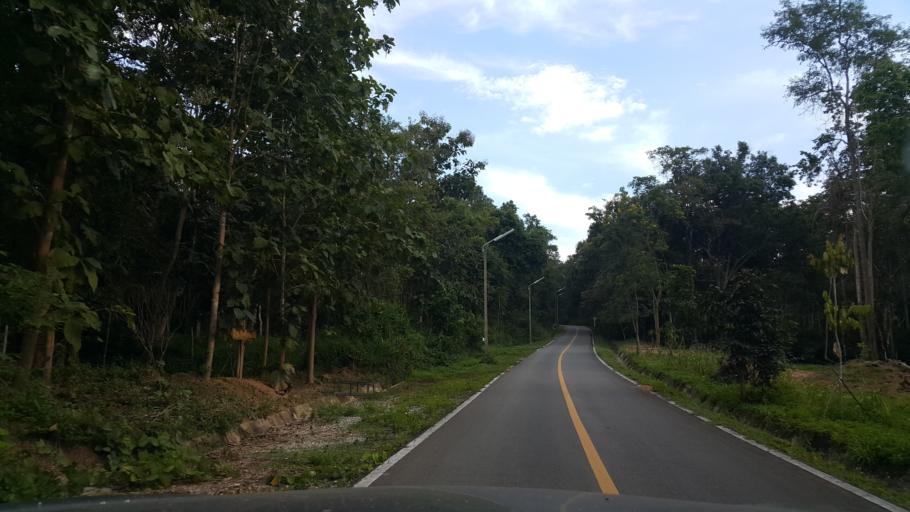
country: TH
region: Chiang Mai
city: San Sai
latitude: 18.9469
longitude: 99.0667
